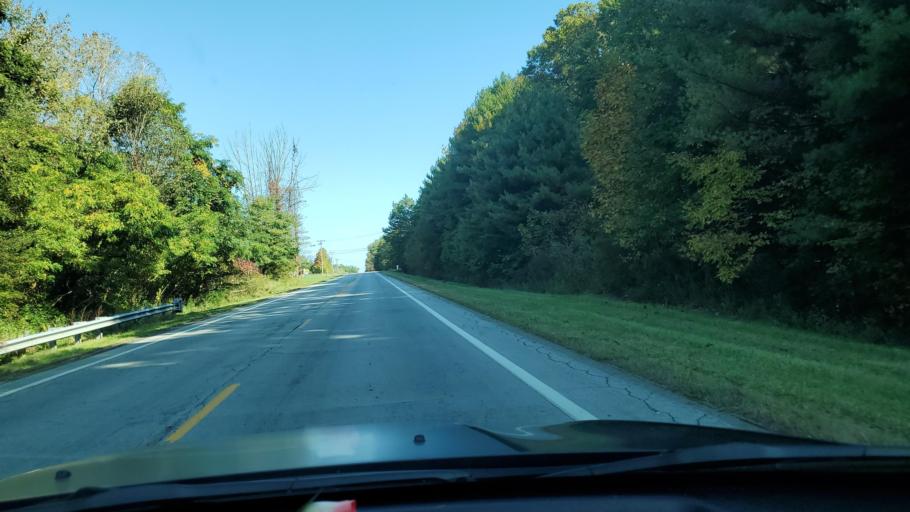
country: US
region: Ohio
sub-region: Trumbull County
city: Brookfield Center
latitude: 41.2806
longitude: -80.5685
